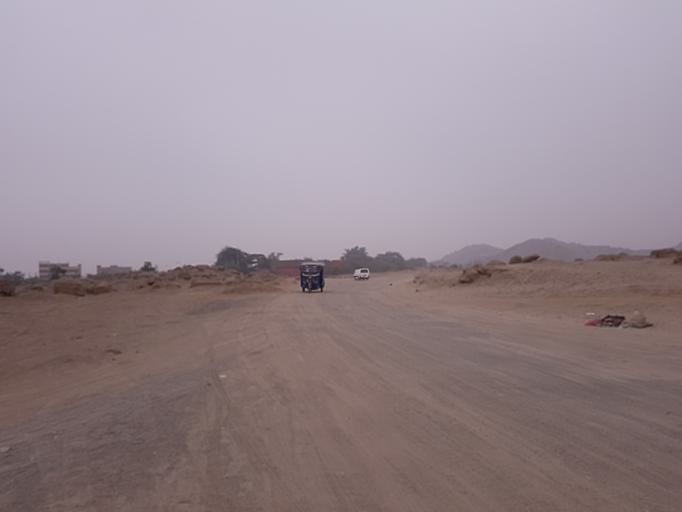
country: PE
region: Lima
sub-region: Lima
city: Santa Maria
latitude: -11.9861
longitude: -76.9124
